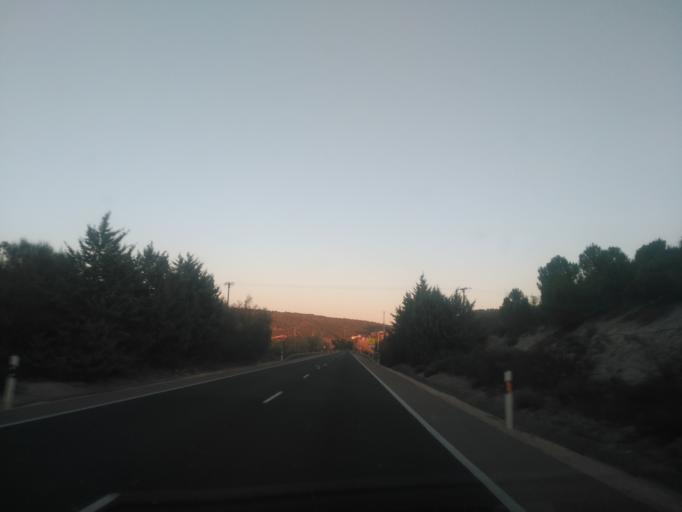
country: ES
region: Castille and Leon
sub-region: Provincia de Valladolid
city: Quintanilla de Onesimo
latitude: 41.6196
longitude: -4.3688
